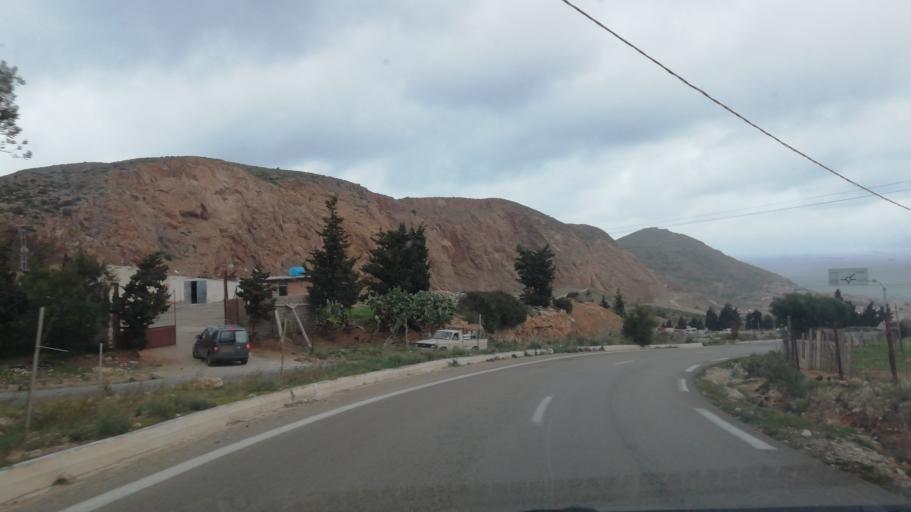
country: DZ
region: Oran
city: Mers el Kebir
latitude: 35.7210
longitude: -0.7354
